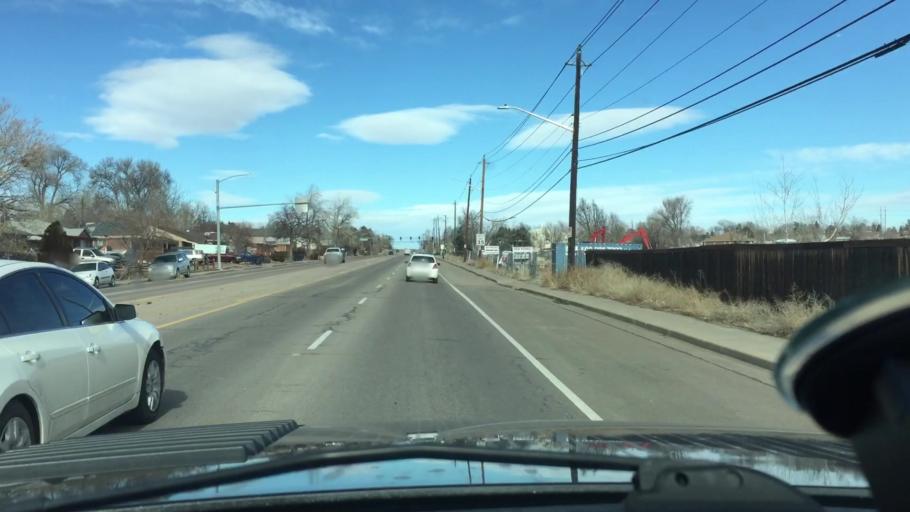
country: US
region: Colorado
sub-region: Adams County
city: Sherrelwood
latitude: 39.8392
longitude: -105.0060
